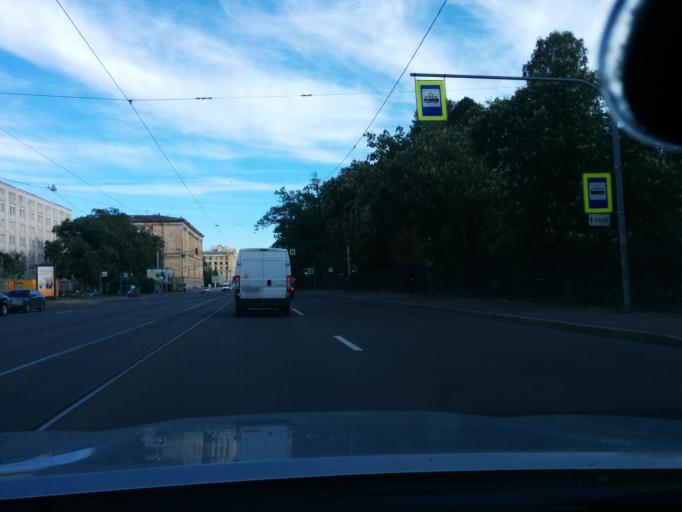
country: RU
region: Leningrad
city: Svetlanovskiy
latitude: 60.0064
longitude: 30.3264
